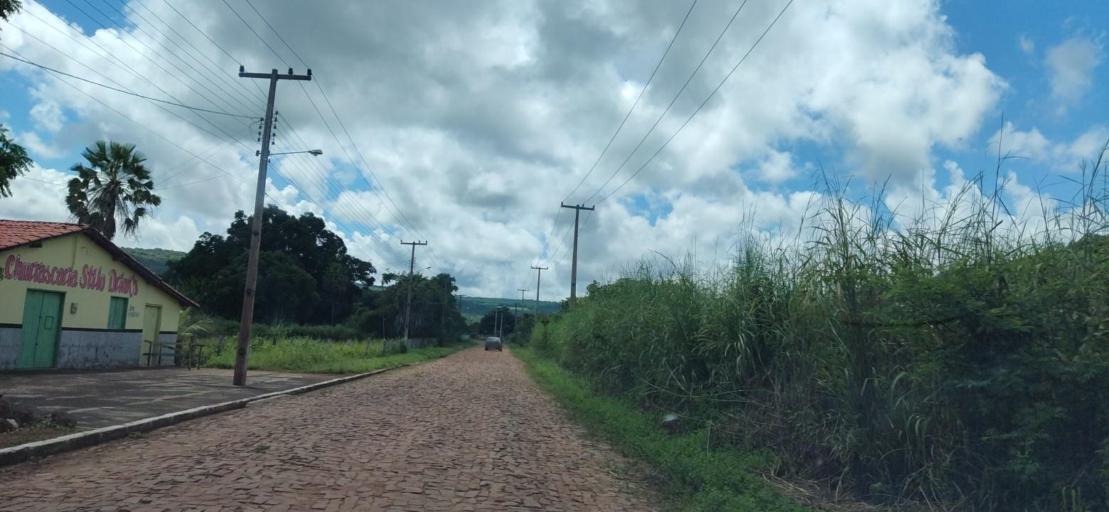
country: BR
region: Piaui
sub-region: Valenca Do Piaui
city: Valenca do Piaui
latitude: -6.1127
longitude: -41.8038
